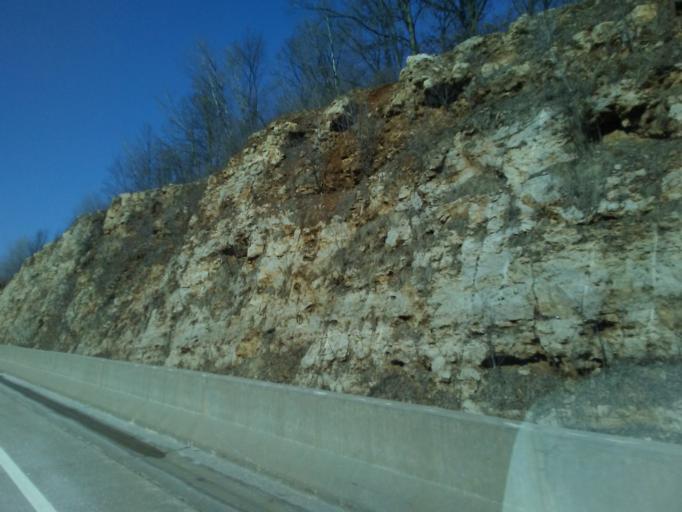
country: US
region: Wisconsin
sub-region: La Crosse County
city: West Salem
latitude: 43.7110
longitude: -91.0632
